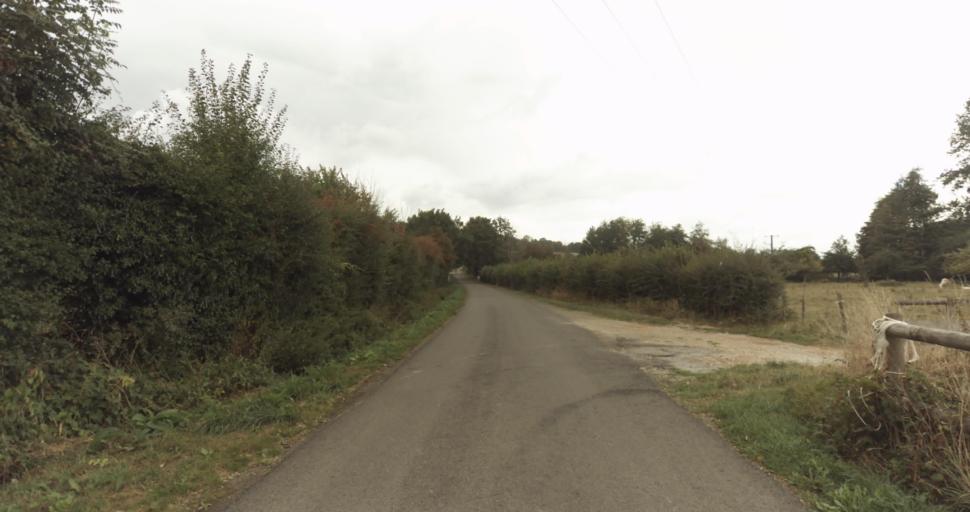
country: FR
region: Lower Normandy
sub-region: Departement de l'Orne
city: Gace
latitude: 48.8702
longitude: 0.2772
